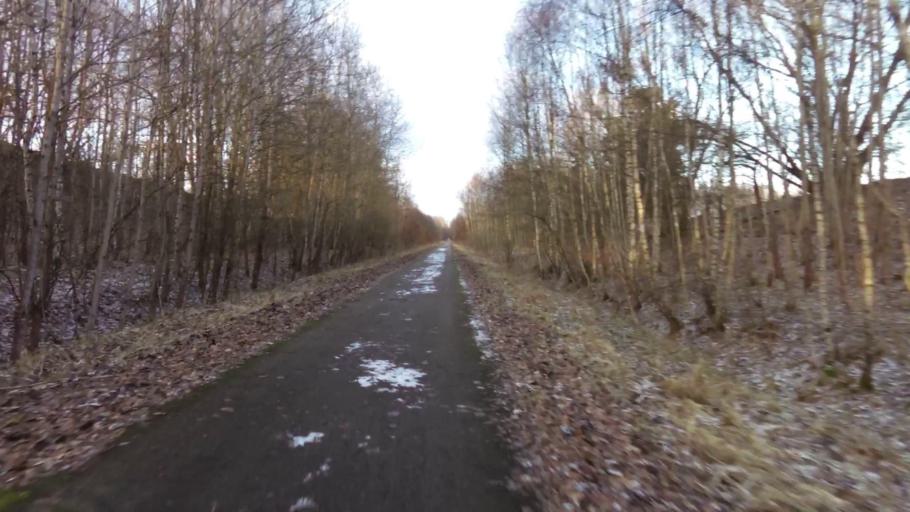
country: PL
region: West Pomeranian Voivodeship
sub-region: Powiat drawski
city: Zlocieniec
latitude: 53.6131
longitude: 16.0517
